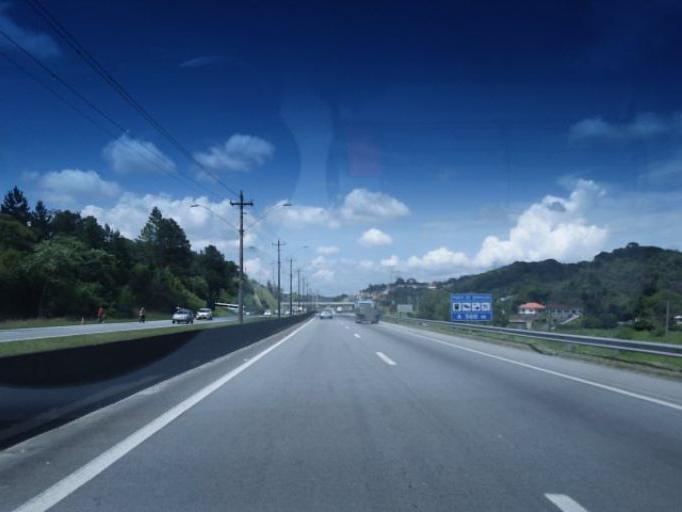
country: BR
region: Sao Paulo
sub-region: Sao Lourenco Da Serra
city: Sao Lourenco da Serra
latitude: -23.8795
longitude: -46.9699
